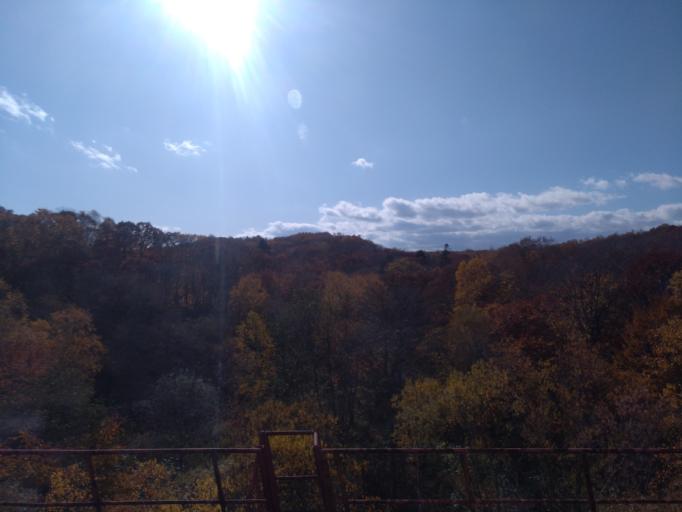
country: JP
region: Hokkaido
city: Kitahiroshima
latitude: 43.0039
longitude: 141.5077
